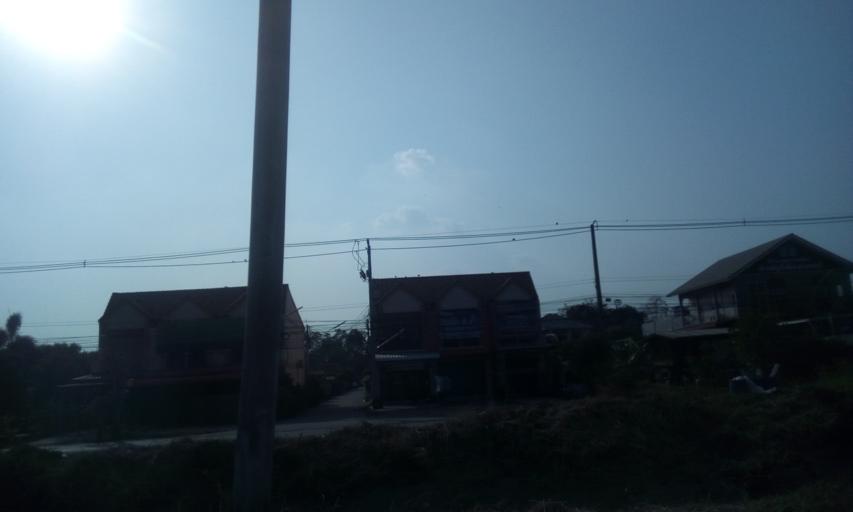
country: TH
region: Sing Buri
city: Sing Buri
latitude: 14.8696
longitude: 100.4051
